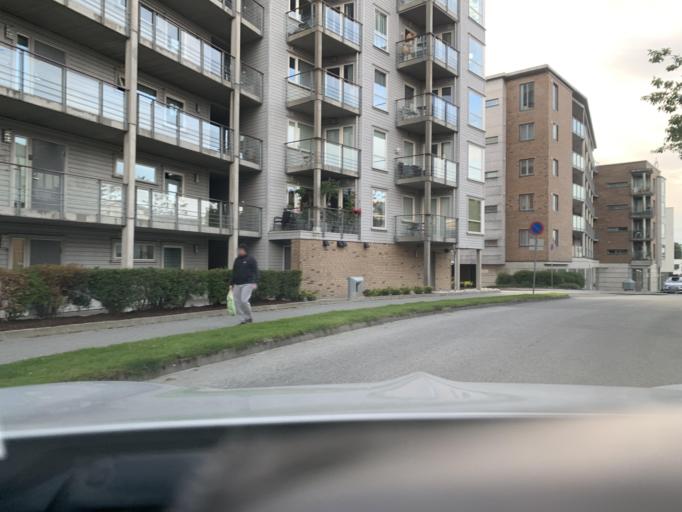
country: NO
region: Rogaland
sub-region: Time
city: Bryne
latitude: 58.7346
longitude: 5.6511
